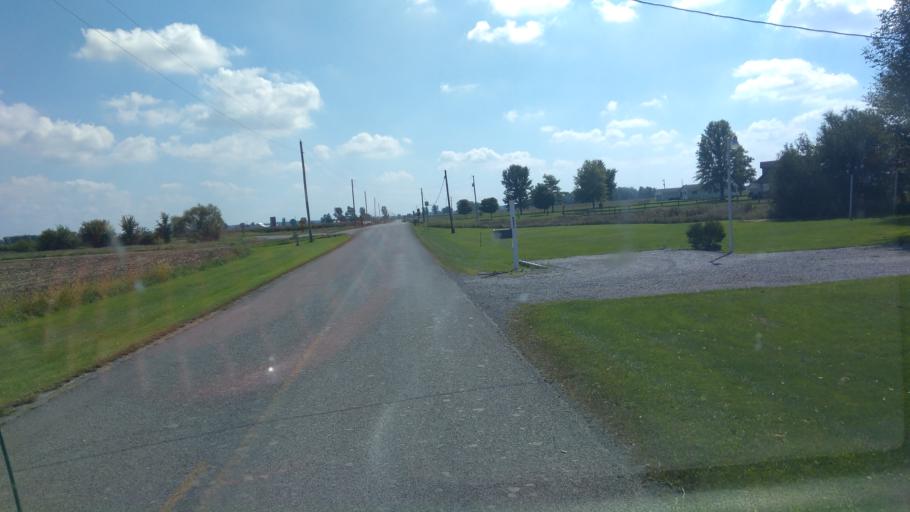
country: US
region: Ohio
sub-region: Hardin County
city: Ada
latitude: 40.6910
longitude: -83.8421
